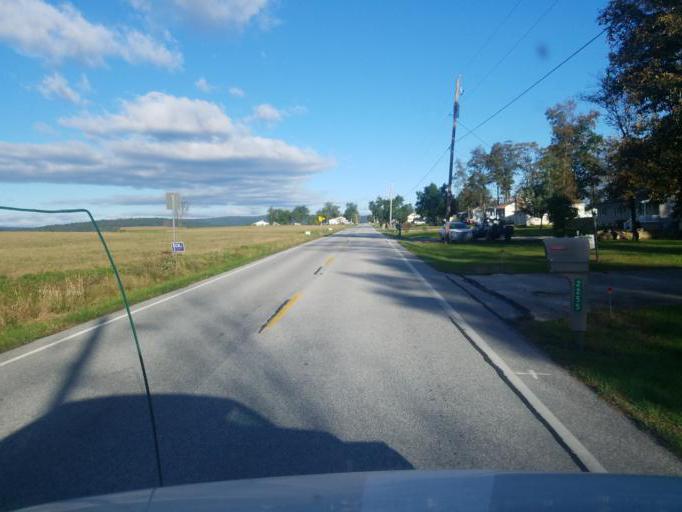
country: US
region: Pennsylvania
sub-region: Adams County
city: Biglerville
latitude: 39.8771
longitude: -77.2812
